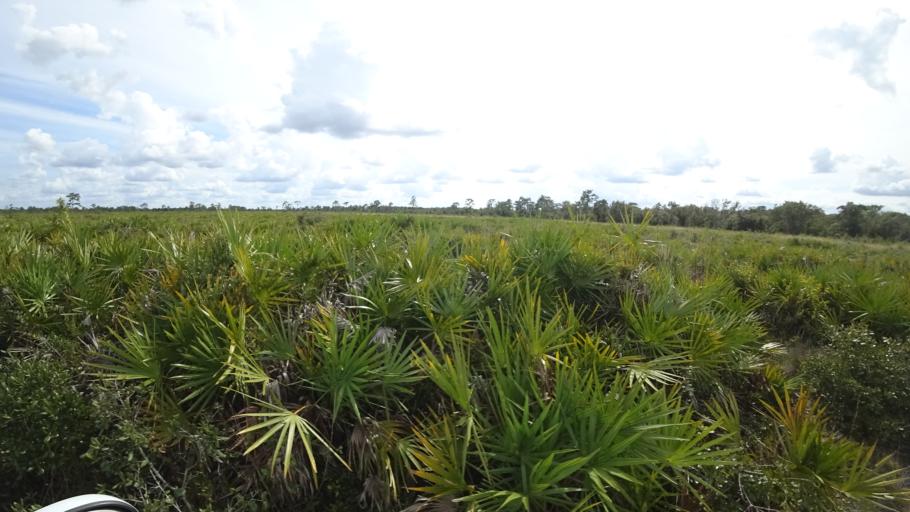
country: US
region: Florida
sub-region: Hillsborough County
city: Wimauma
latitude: 27.5603
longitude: -82.1465
